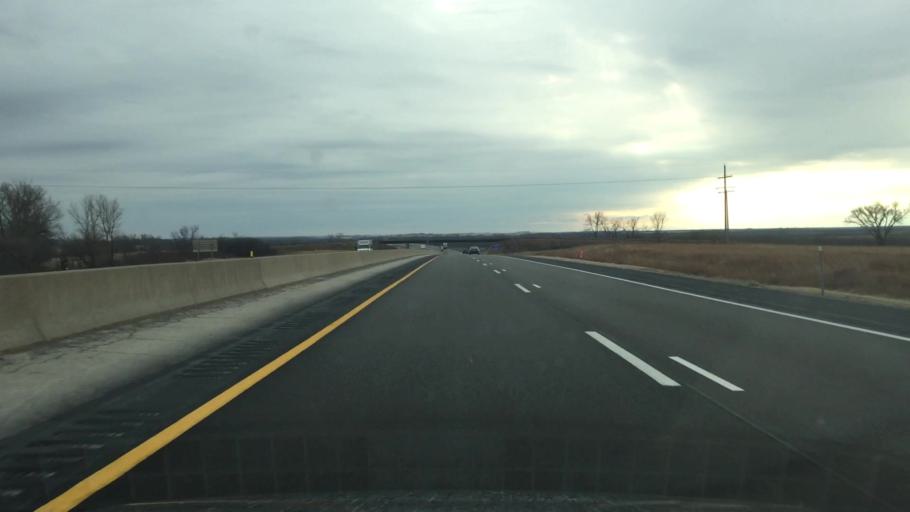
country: US
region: Kansas
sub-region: Osage County
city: Osage City
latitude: 38.6381
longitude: -96.0393
